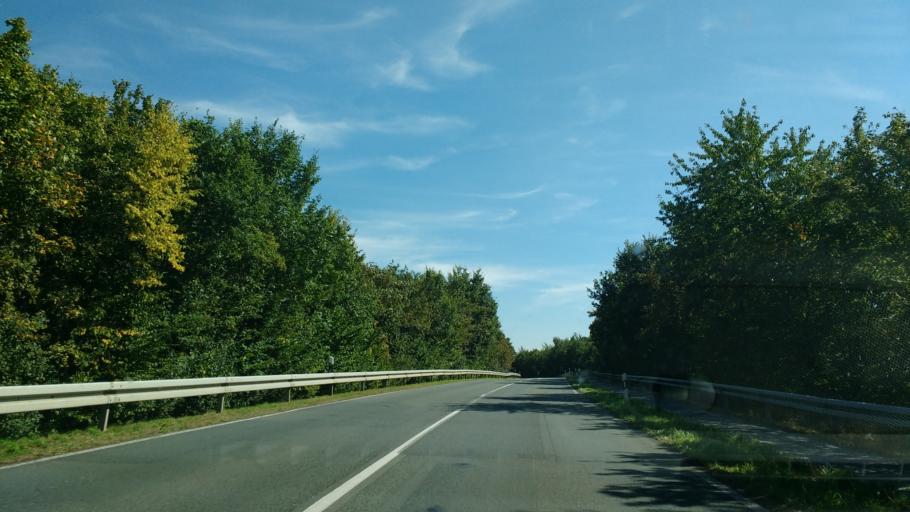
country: DE
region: North Rhine-Westphalia
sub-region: Regierungsbezirk Detmold
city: Langenberg
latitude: 51.8143
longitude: 8.3260
